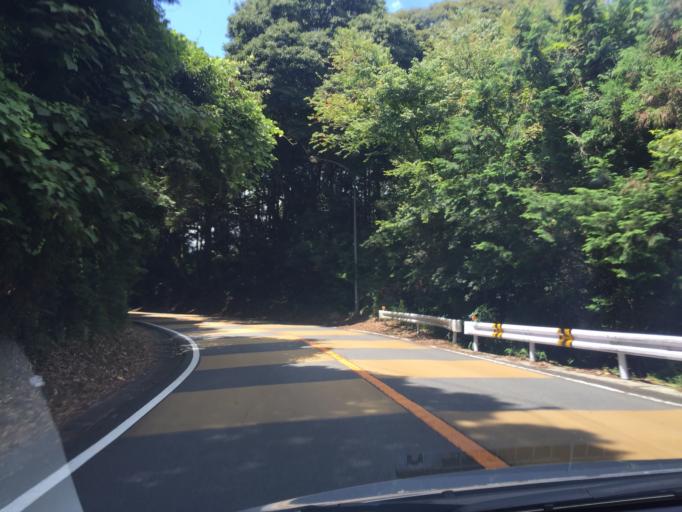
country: JP
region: Shizuoka
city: Kanaya
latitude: 34.8184
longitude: 138.1209
